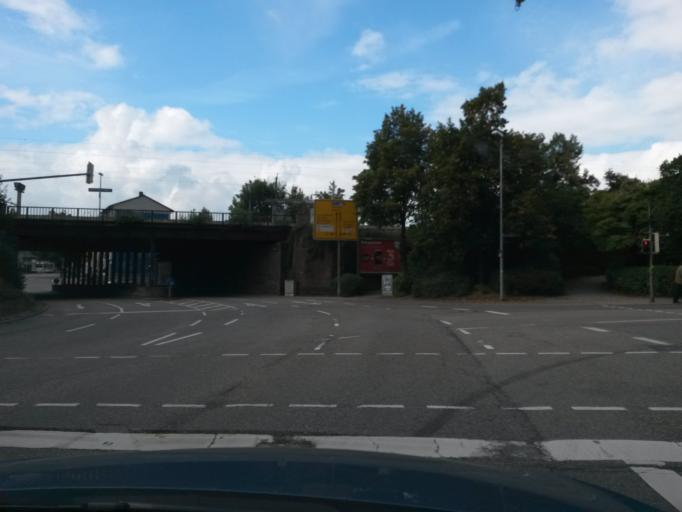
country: DE
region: Baden-Wuerttemberg
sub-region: Karlsruhe Region
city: Ispringen
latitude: 48.8893
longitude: 8.6677
